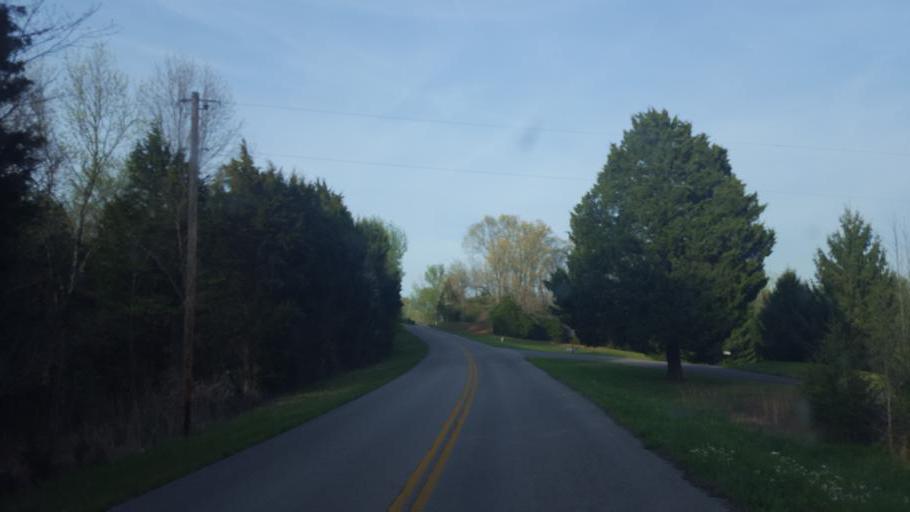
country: US
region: Kentucky
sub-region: Allen County
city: Scottsville
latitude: 36.9092
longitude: -86.1113
